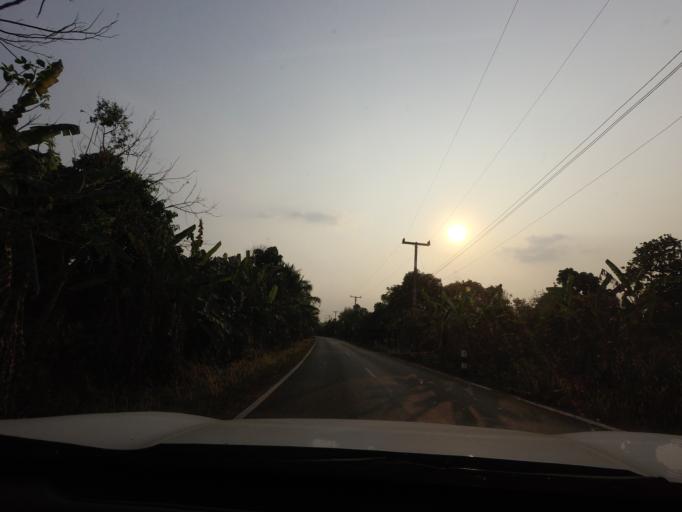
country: TH
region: Nakhon Nayok
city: Pak Phli
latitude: 14.1563
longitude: 101.3575
